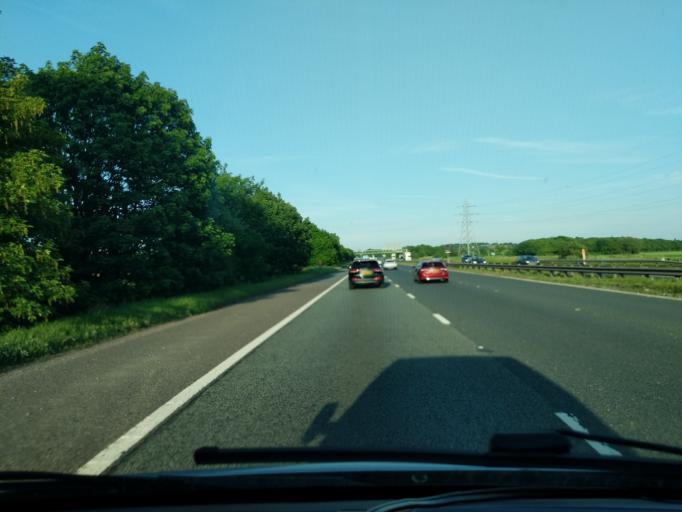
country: GB
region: England
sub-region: Knowsley
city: Whiston
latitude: 53.4011
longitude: -2.7839
